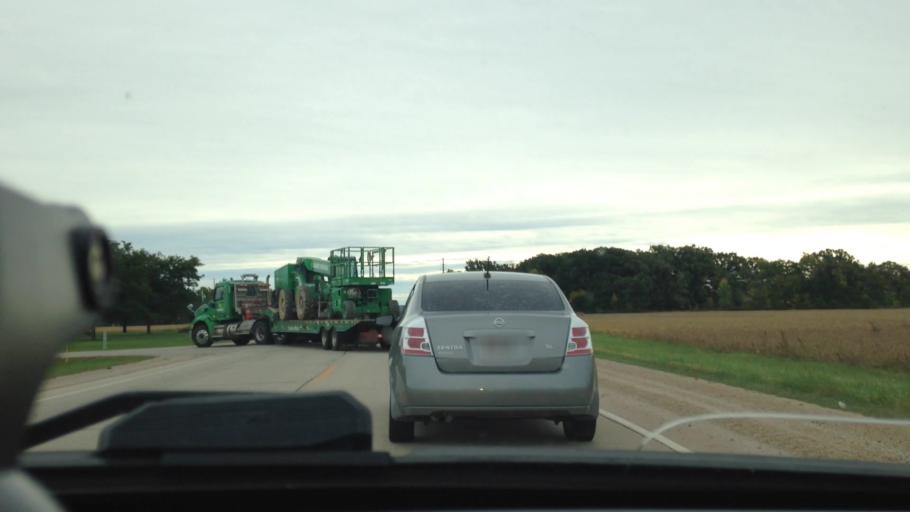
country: US
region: Wisconsin
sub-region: Fond du Lac County
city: North Fond du Lac
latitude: 43.8022
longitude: -88.4977
